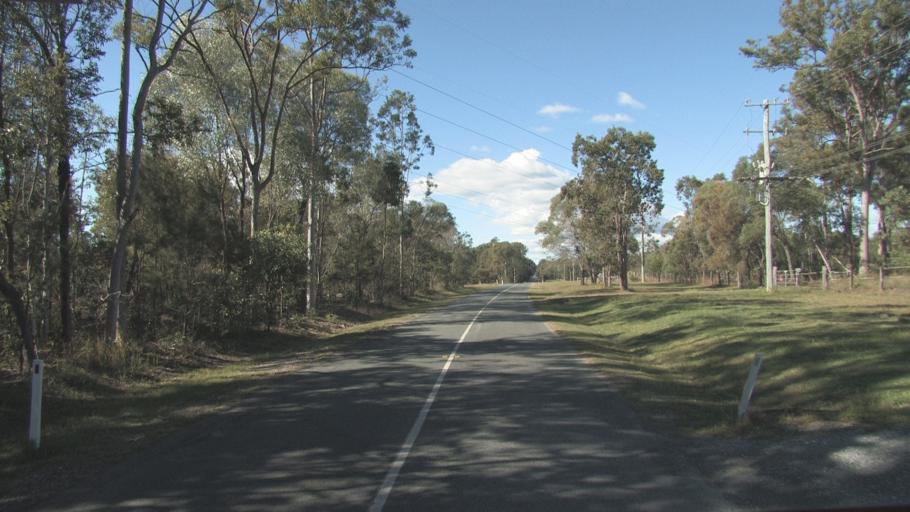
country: AU
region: Queensland
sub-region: Logan
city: Chambers Flat
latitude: -27.7925
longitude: 153.0728
